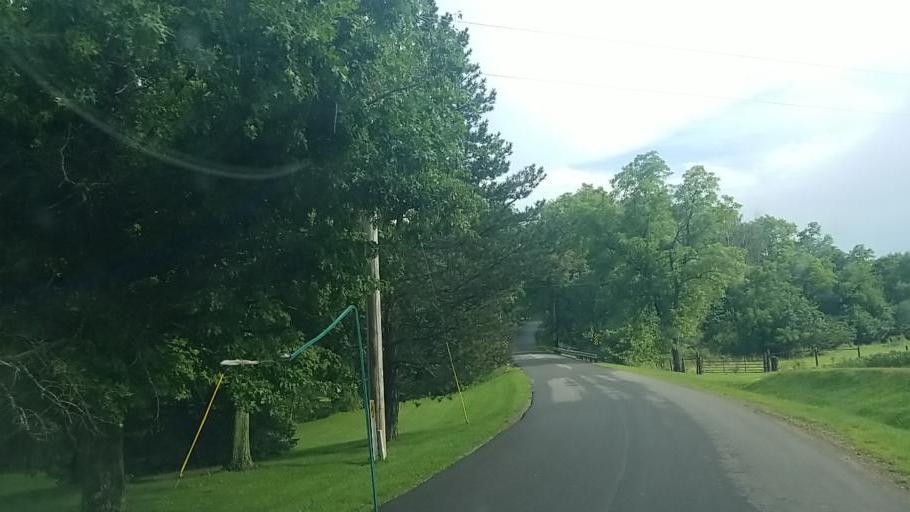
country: US
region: Ohio
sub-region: Wayne County
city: Creston
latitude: 40.9490
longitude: -81.9375
